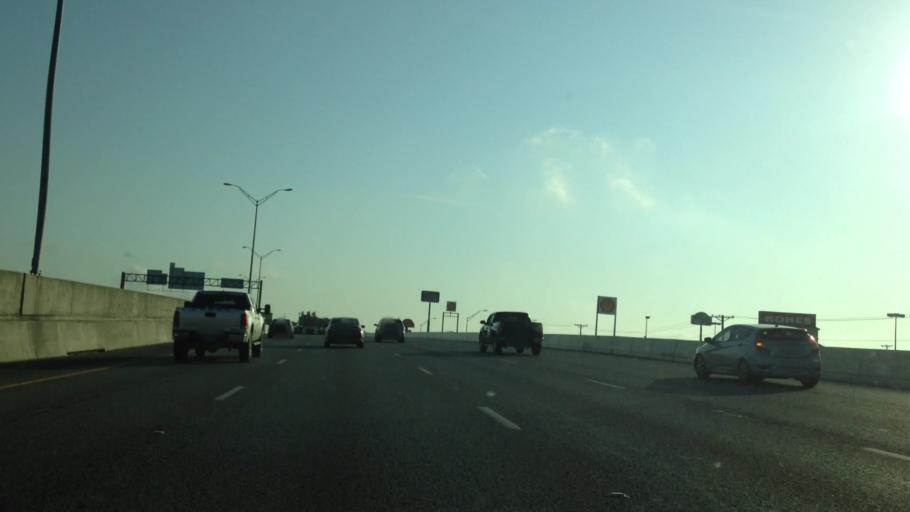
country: US
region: Texas
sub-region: Comal County
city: New Braunfels
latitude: 29.6968
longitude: -98.0952
